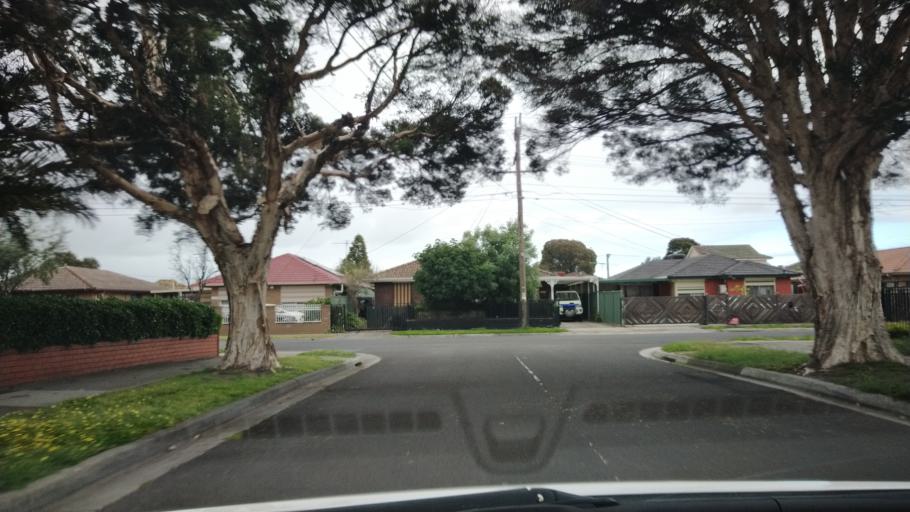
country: AU
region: Victoria
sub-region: Greater Dandenong
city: Keysborough
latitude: -37.9818
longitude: 145.1729
